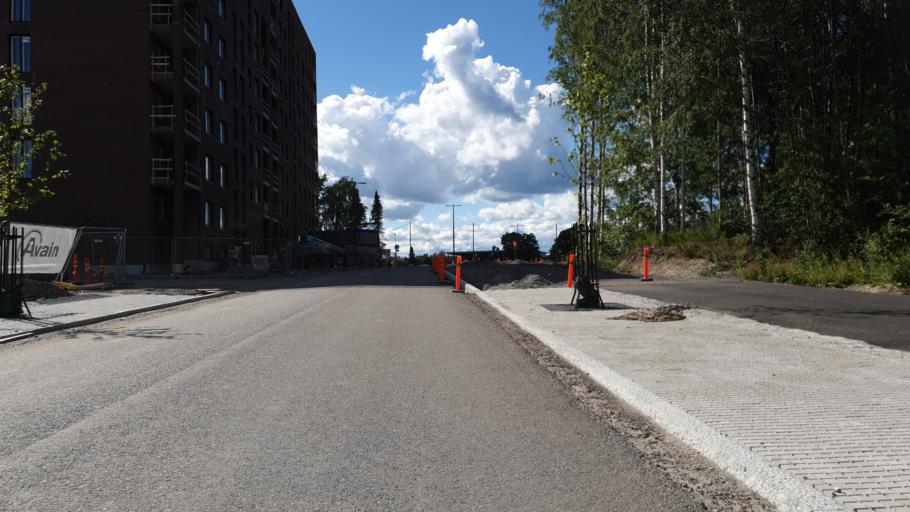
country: FI
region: Uusimaa
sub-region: Helsinki
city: Tuusula
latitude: 60.3996
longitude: 25.0354
